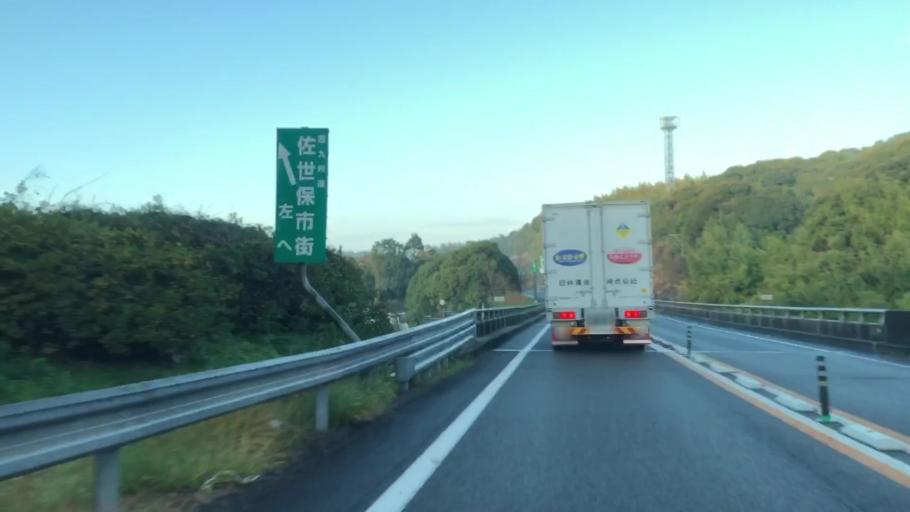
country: JP
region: Nagasaki
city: Sasebo
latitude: 33.1502
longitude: 129.7887
